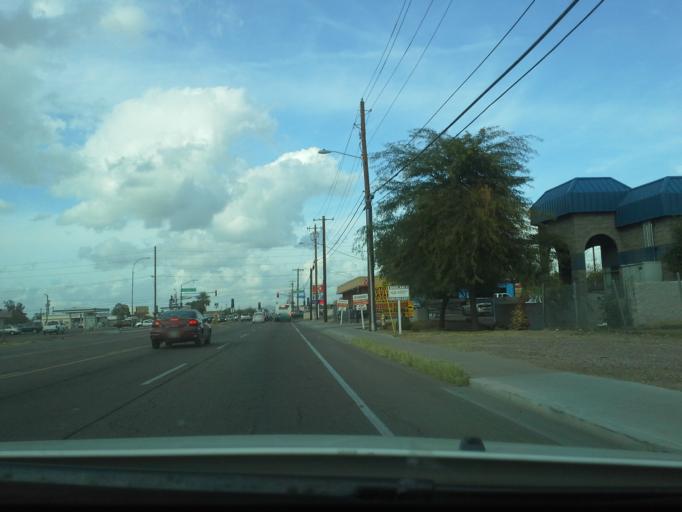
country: US
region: Arizona
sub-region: Maricopa County
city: Phoenix
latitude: 33.4052
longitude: -112.0820
